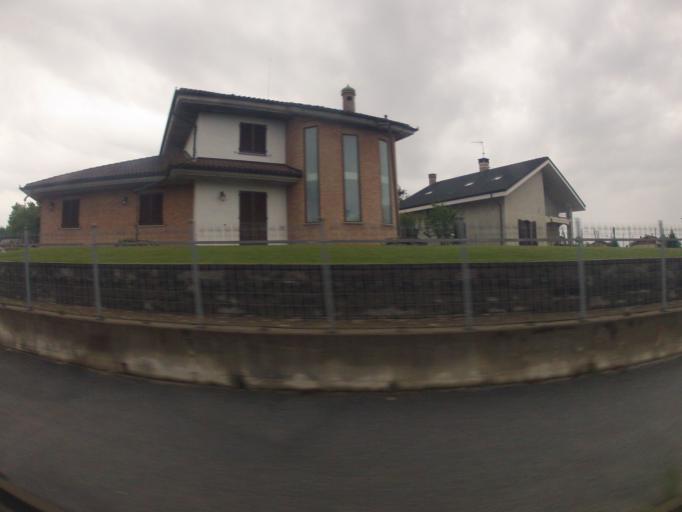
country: IT
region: Piedmont
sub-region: Provincia di Cuneo
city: Casalgrasso
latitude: 44.8201
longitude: 7.6230
